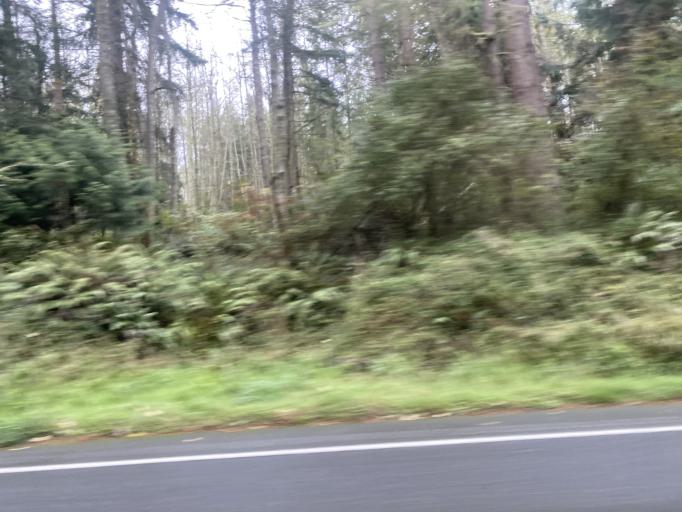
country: US
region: Washington
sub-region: Island County
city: Freeland
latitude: 48.0499
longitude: -122.5068
